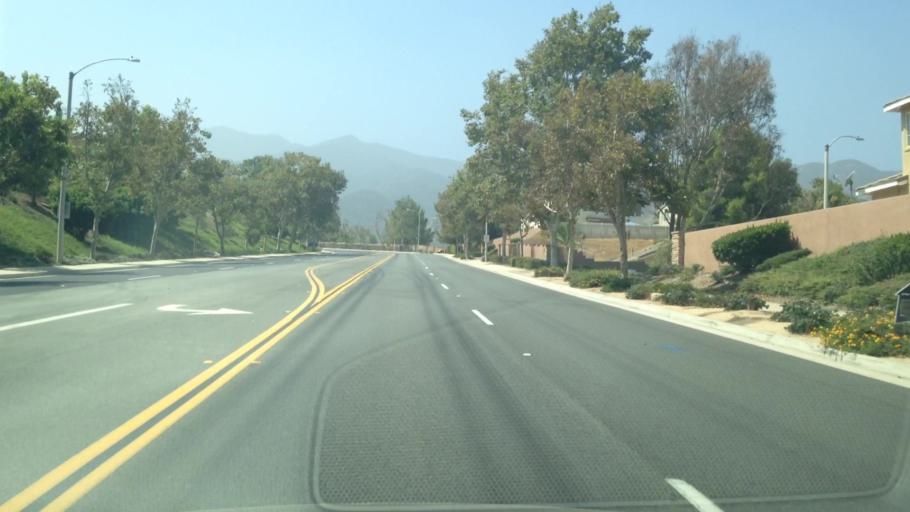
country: US
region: California
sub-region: Riverside County
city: El Cerrito
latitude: 33.7881
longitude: -117.5005
